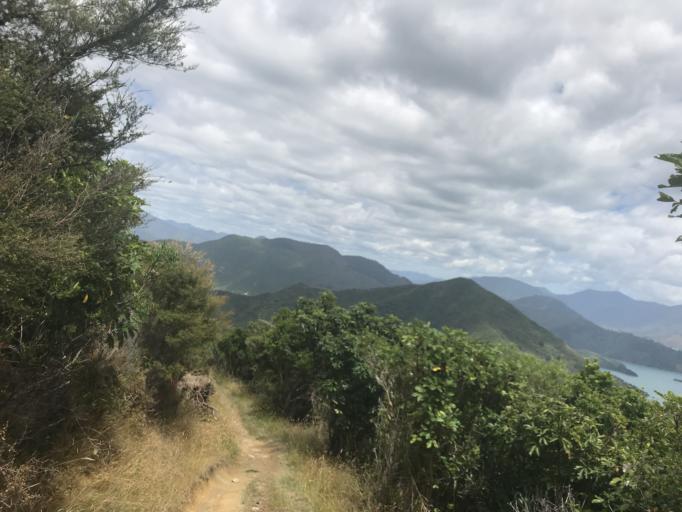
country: NZ
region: Marlborough
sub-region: Marlborough District
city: Picton
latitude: -41.2126
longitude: 174.0106
